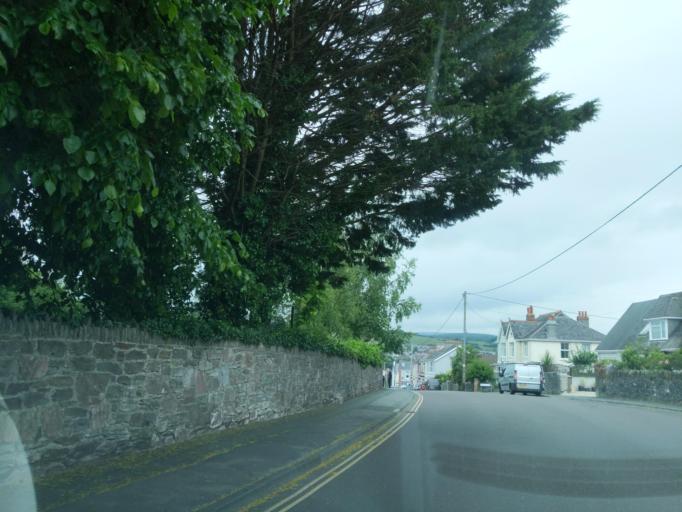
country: GB
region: England
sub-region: Devon
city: Plympton
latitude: 50.3890
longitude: -4.0499
